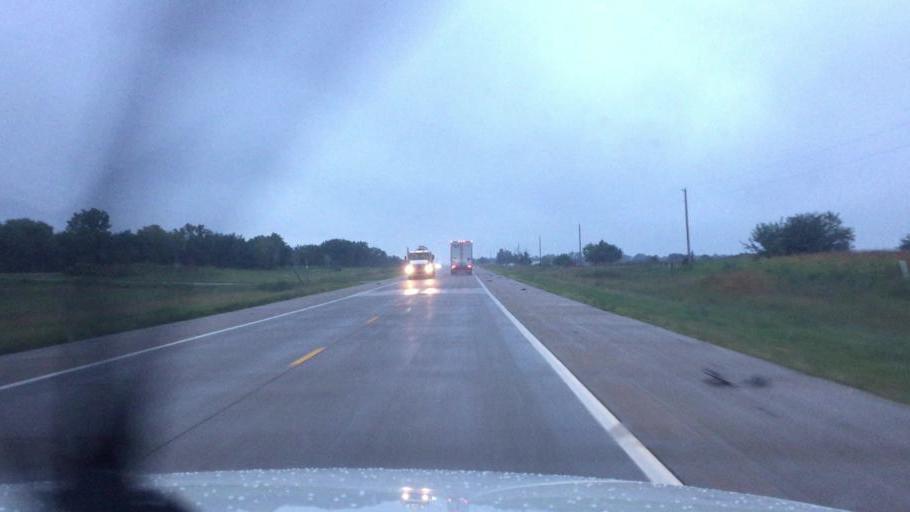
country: US
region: Kansas
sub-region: Neosho County
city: Chanute
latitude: 37.5080
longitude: -95.4709
